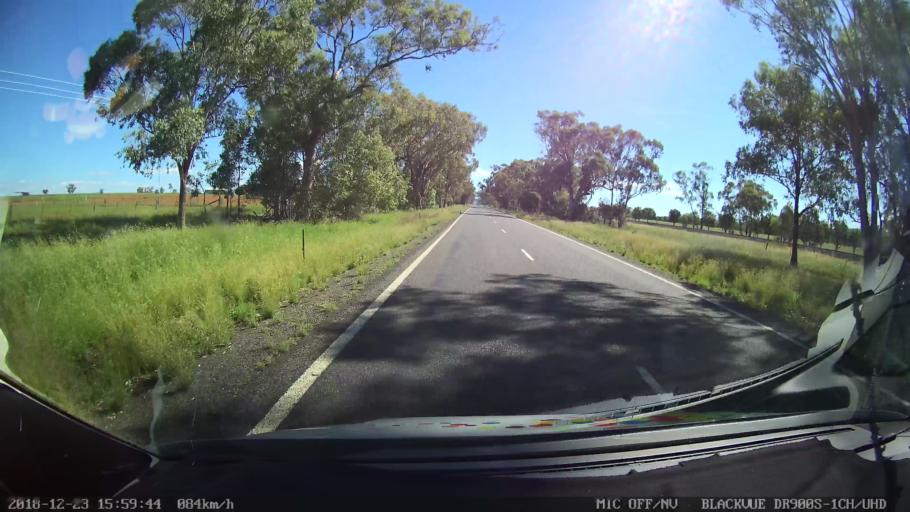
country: AU
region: New South Wales
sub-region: Tamworth Municipality
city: Phillip
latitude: -31.2030
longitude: 150.8308
